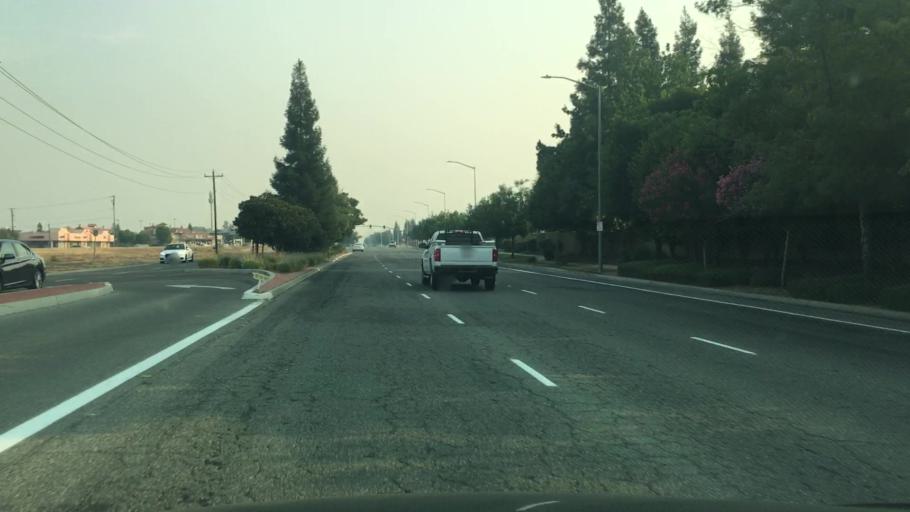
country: US
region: California
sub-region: Fresno County
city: Clovis
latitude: 36.8424
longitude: -119.7296
